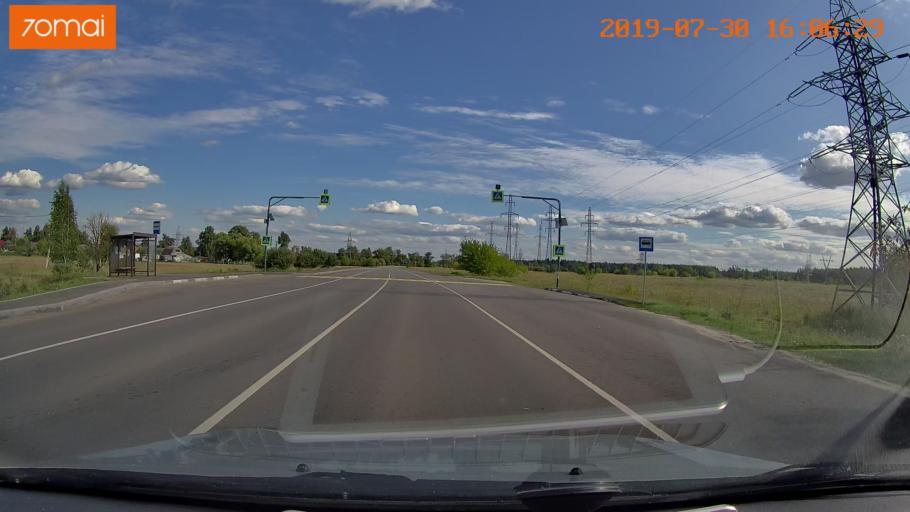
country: RU
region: Moskovskaya
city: Peski
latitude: 55.2555
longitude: 38.7168
